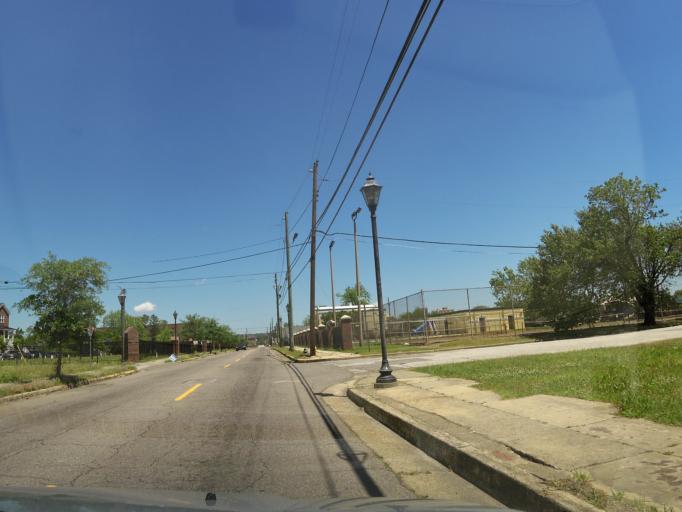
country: US
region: Georgia
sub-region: Richmond County
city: Augusta
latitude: 33.4661
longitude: -81.9727
